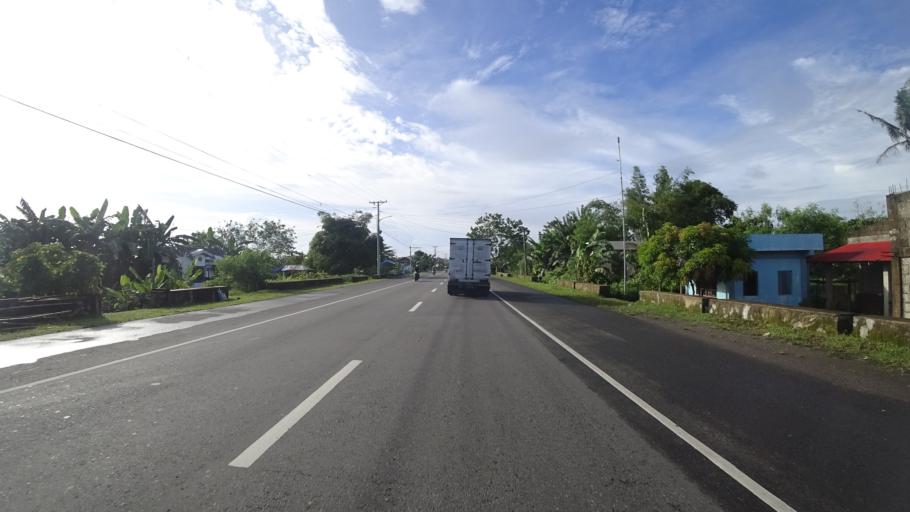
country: PH
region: Eastern Visayas
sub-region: Province of Leyte
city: Tanauan
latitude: 11.1249
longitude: 125.0129
